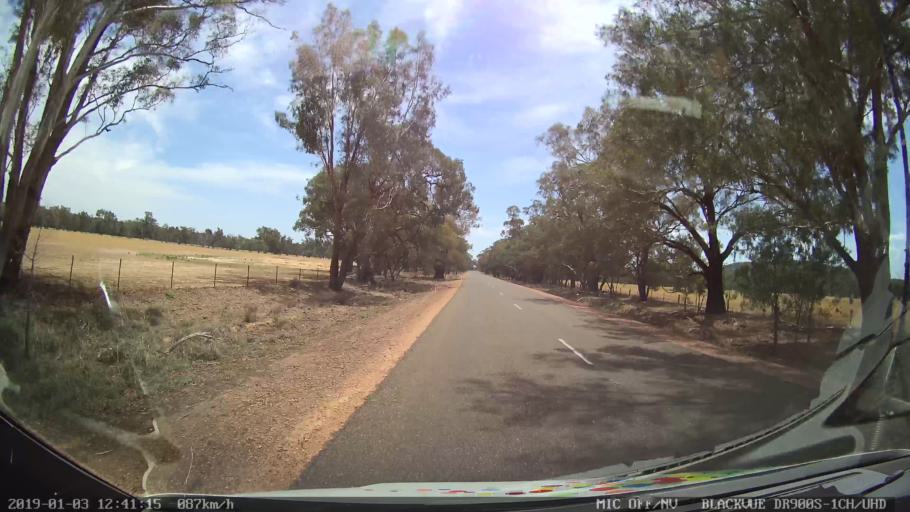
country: AU
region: New South Wales
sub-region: Weddin
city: Grenfell
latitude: -33.8020
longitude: 148.2147
